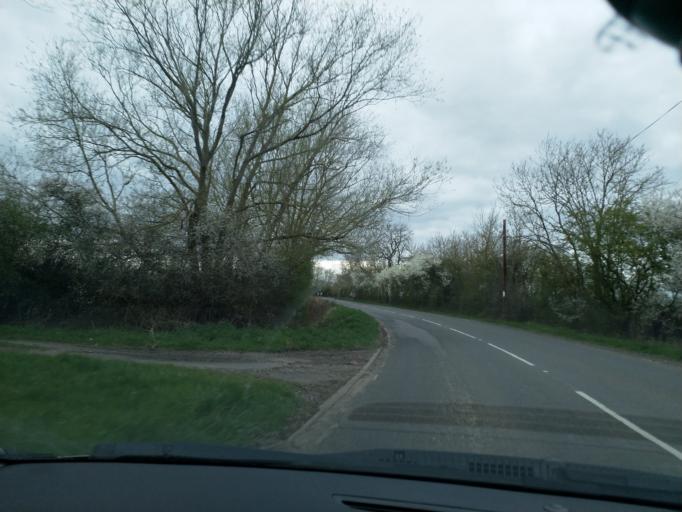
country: GB
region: England
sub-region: Warwickshire
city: Harbury
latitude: 52.1486
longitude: -1.4734
